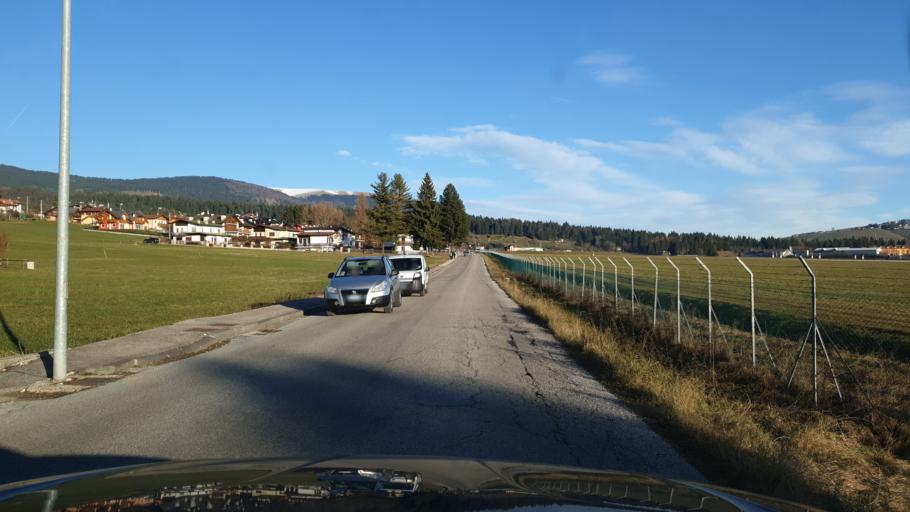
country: IT
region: Veneto
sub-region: Provincia di Vicenza
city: Asiago
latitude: 45.8870
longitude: 11.5103
